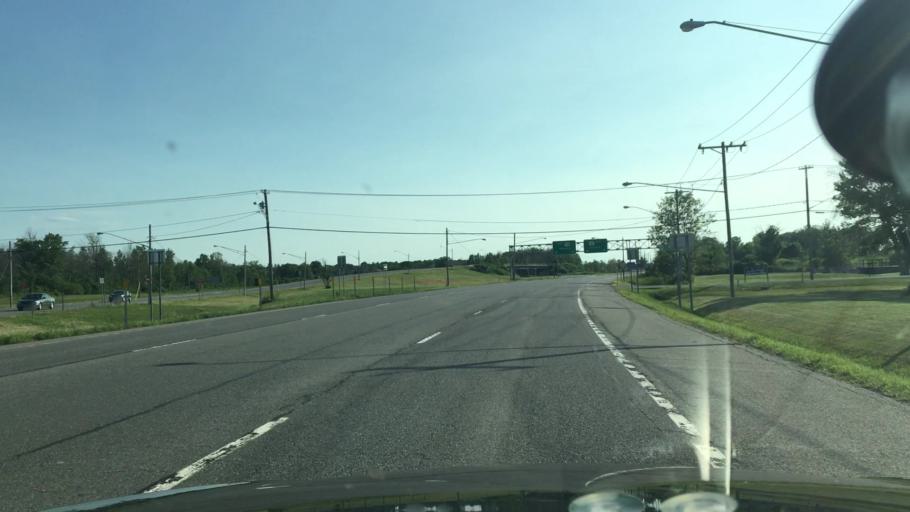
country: US
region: New York
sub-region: Erie County
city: Blasdell
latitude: 42.7805
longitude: -78.8531
